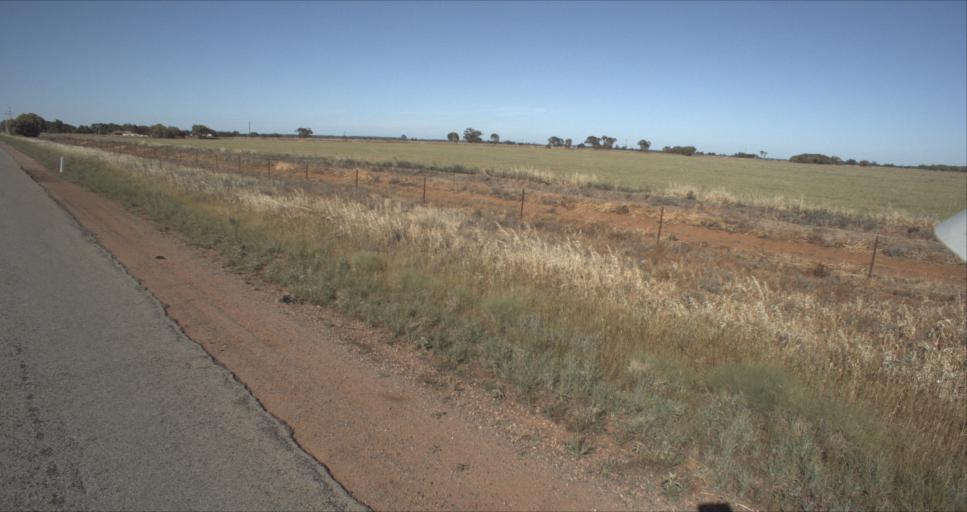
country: AU
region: New South Wales
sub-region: Leeton
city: Leeton
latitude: -34.5640
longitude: 146.3122
